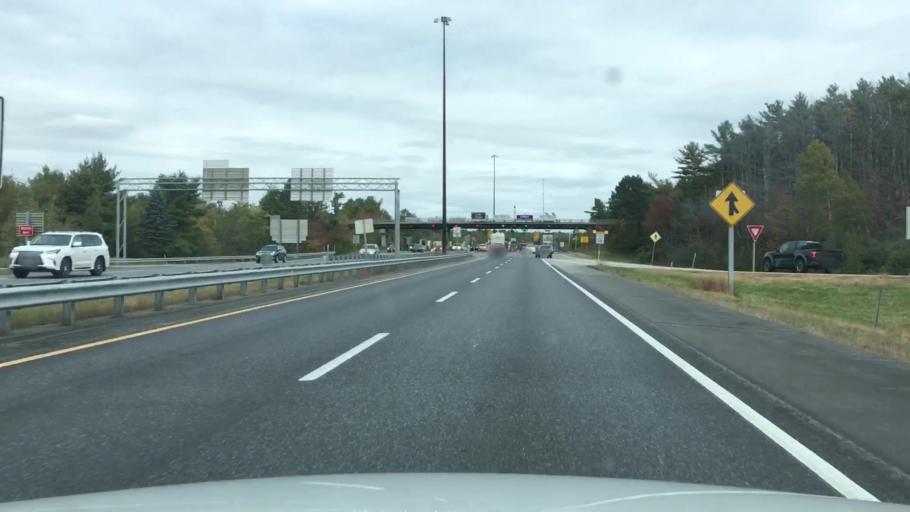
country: US
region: Maine
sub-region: Kennebec County
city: Gardiner
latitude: 44.2109
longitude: -69.8244
